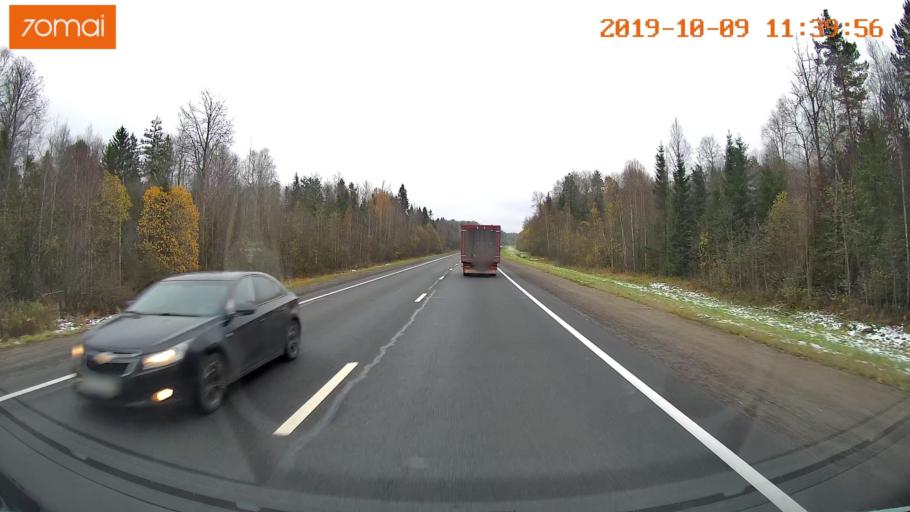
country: RU
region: Vologda
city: Gryazovets
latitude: 58.9500
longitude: 40.1709
